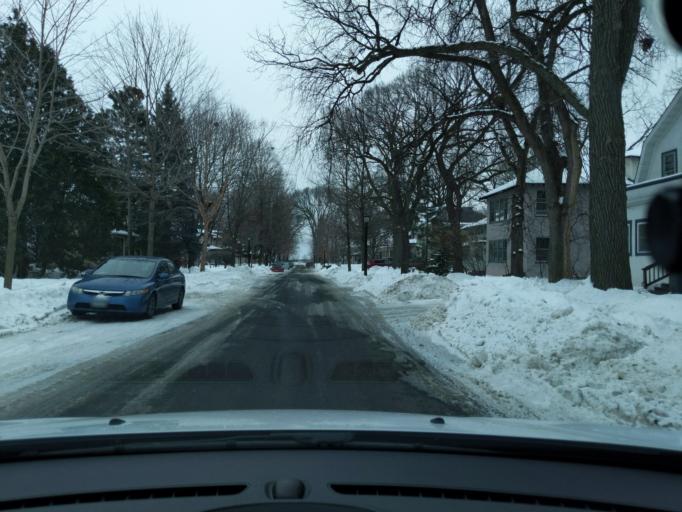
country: US
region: Minnesota
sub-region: Ramsey County
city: Lauderdale
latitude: 44.9627
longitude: -93.2090
